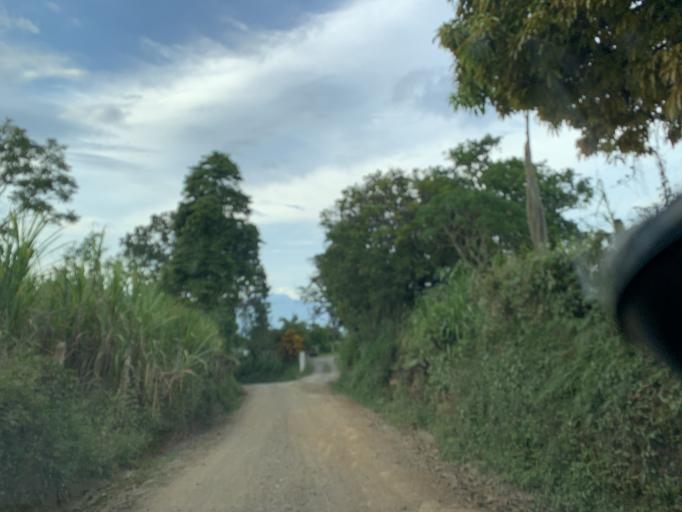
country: CO
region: Boyaca
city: Santana
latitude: 6.0669
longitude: -73.4835
